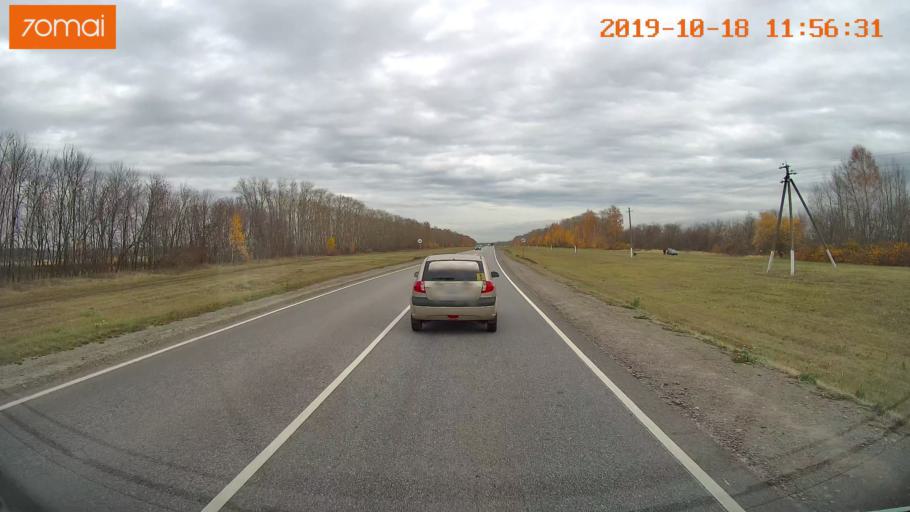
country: RU
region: Rjazan
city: Mikhaylov
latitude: 54.2657
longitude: 39.1209
